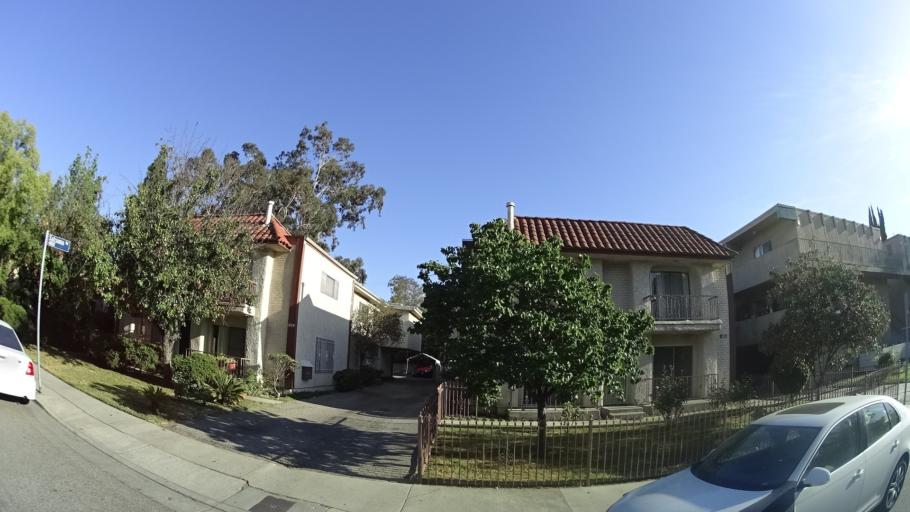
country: US
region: California
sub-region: Los Angeles County
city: North Hollywood
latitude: 34.1577
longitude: -118.3670
